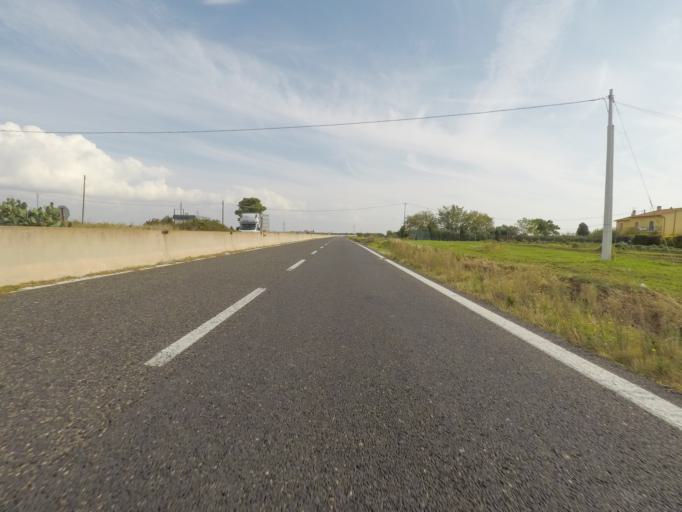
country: IT
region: Latium
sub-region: Provincia di Viterbo
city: Montalto di Castro
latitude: 42.3645
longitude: 11.5790
